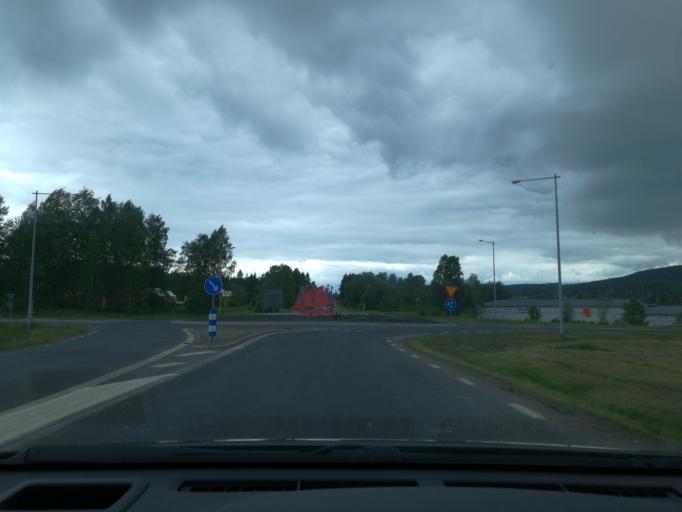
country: SE
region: Dalarna
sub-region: Smedjebackens Kommun
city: Smedjebacken
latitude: 60.1318
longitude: 15.4009
